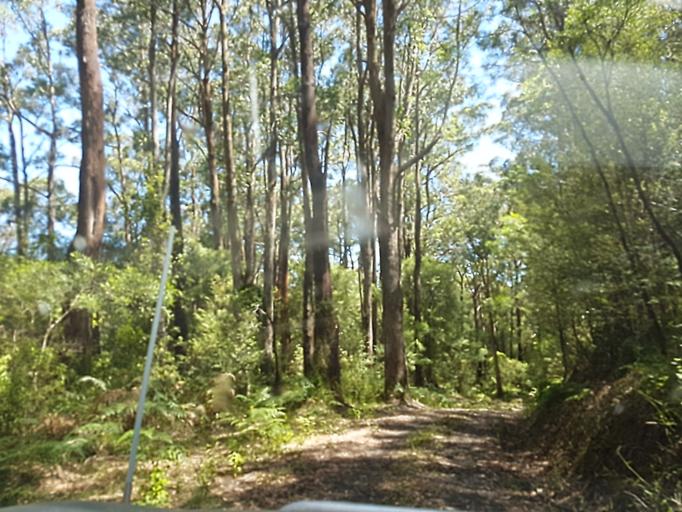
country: AU
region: Victoria
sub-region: Colac-Otway
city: Apollo Bay
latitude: -38.6762
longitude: 143.3460
